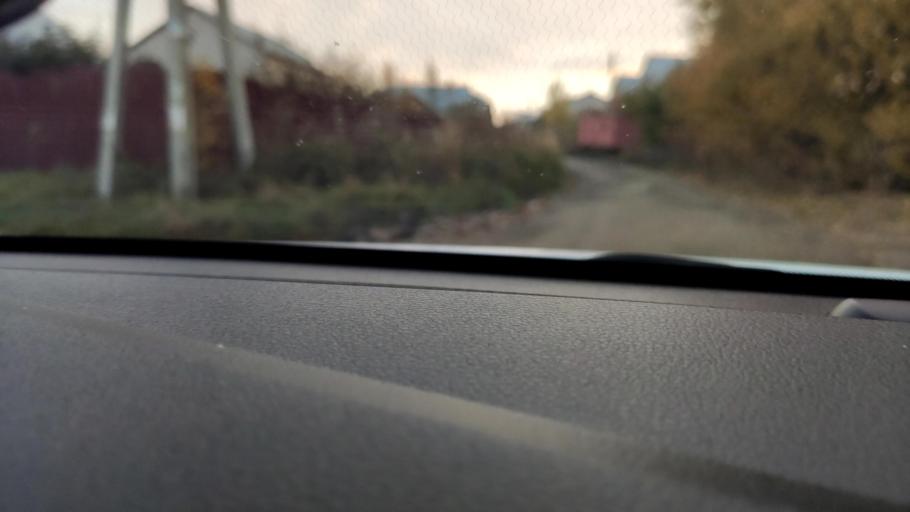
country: RU
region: Tatarstan
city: Stolbishchi
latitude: 55.7589
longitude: 49.2482
